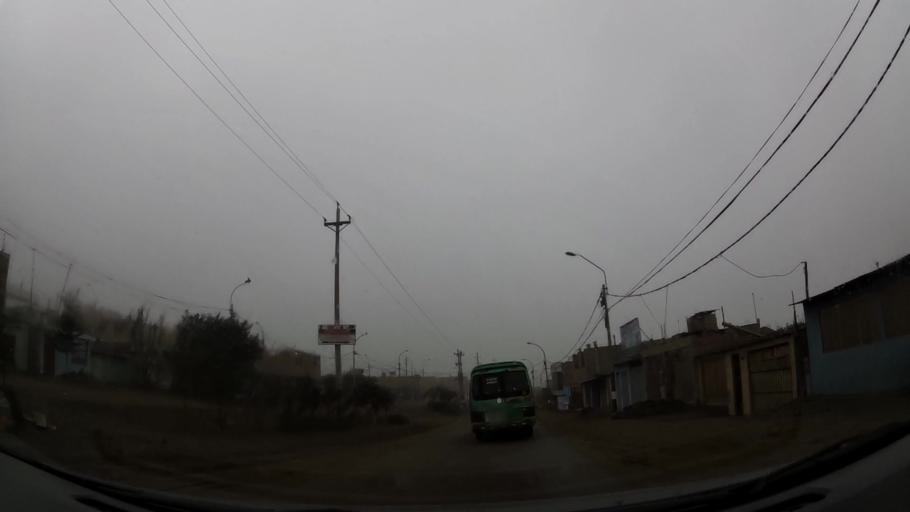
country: PE
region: Lima
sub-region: Lima
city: Santa Rosa
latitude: -11.8299
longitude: -77.1377
